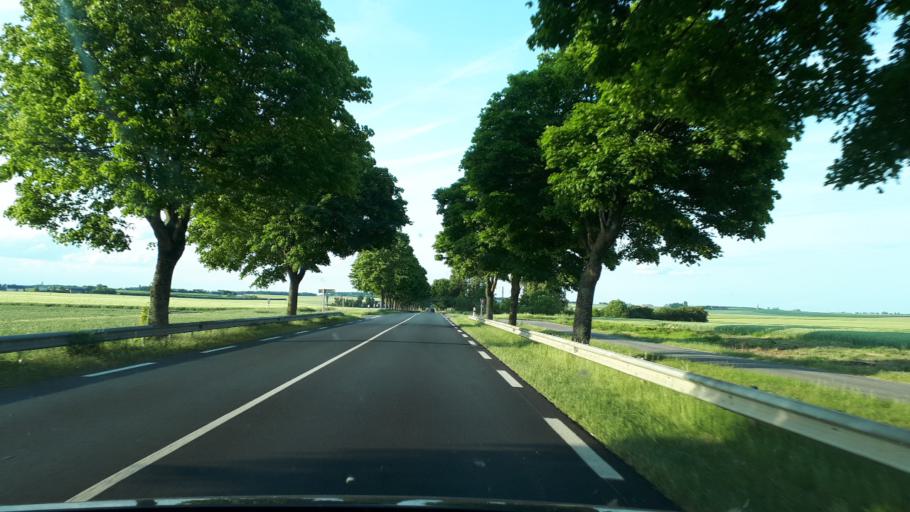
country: FR
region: Centre
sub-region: Departement du Loir-et-Cher
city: Naveil
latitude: 47.7402
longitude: 1.0348
